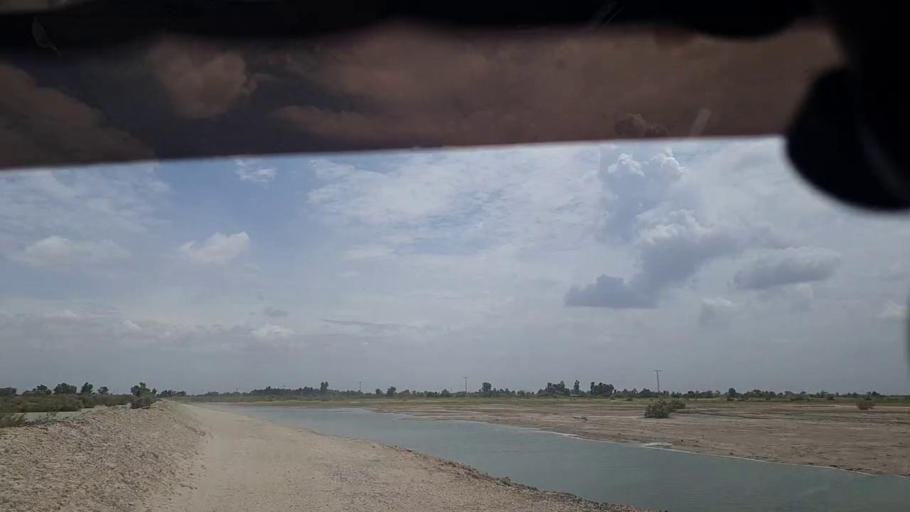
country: PK
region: Sindh
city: Rustam jo Goth
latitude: 28.0294
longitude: 68.9352
